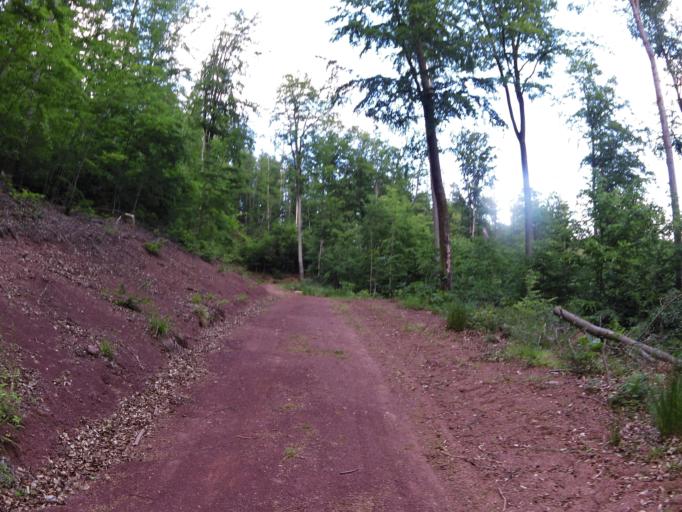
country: DE
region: Thuringia
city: Wolfsburg-Unkeroda
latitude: 50.9251
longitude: 10.3053
